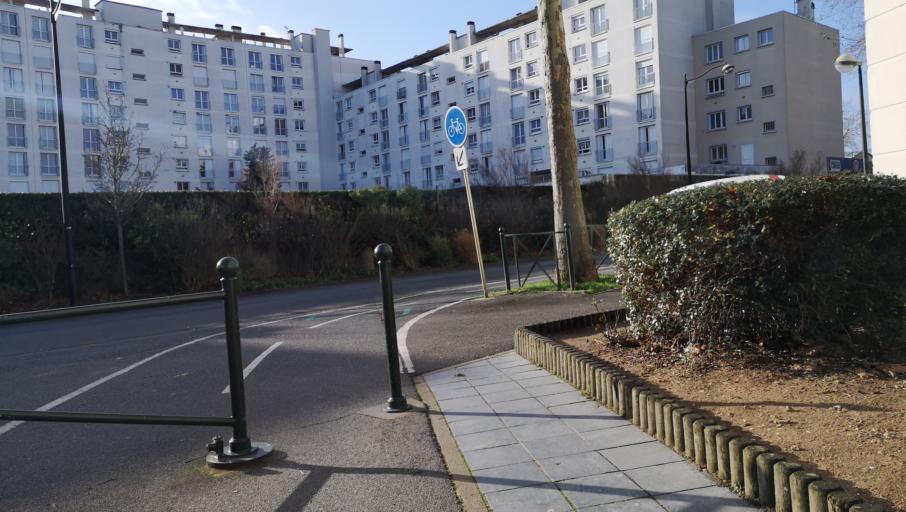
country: FR
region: Centre
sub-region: Departement du Loiret
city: Saint-Jean-le-Blanc
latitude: 47.8890
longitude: 1.9066
